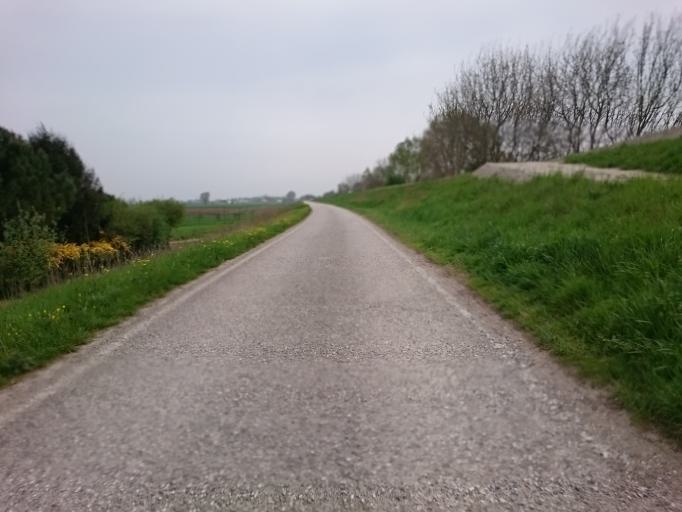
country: IT
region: Veneto
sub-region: Provincia di Rovigo
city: San Martino di Venezze
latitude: 45.1484
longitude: 11.8468
